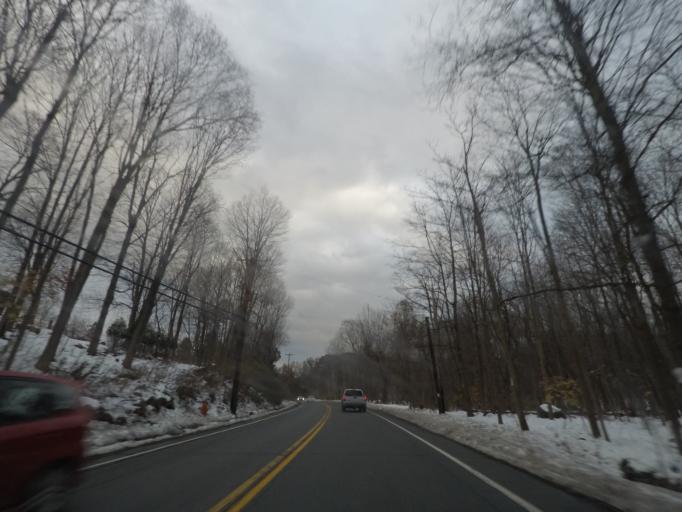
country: US
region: New York
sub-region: Orange County
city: Balmville
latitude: 41.5320
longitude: -74.0382
